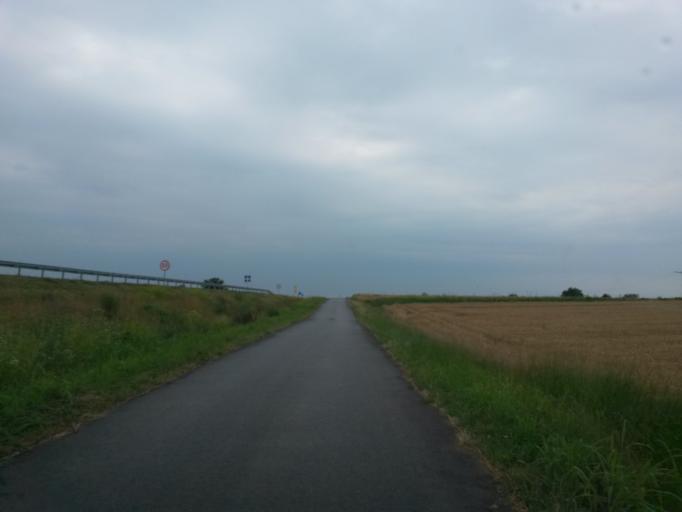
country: HR
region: Vukovarsko-Srijemska
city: Ilok
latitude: 45.2183
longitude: 19.3553
